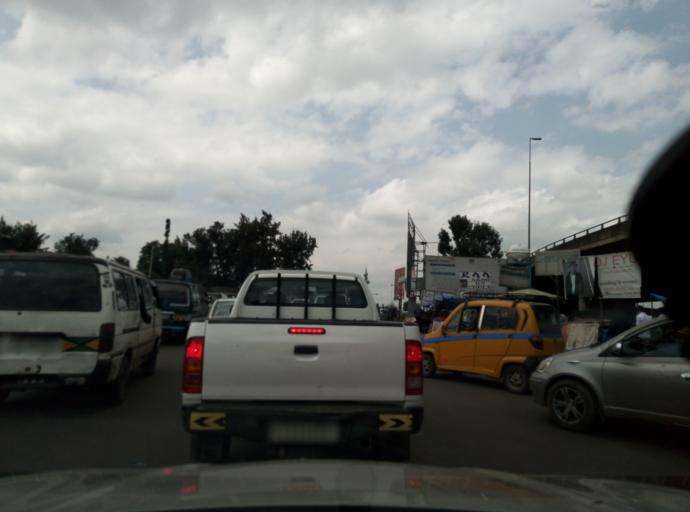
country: ET
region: Adis Abeba
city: Addis Ababa
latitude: 9.0117
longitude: 38.7212
